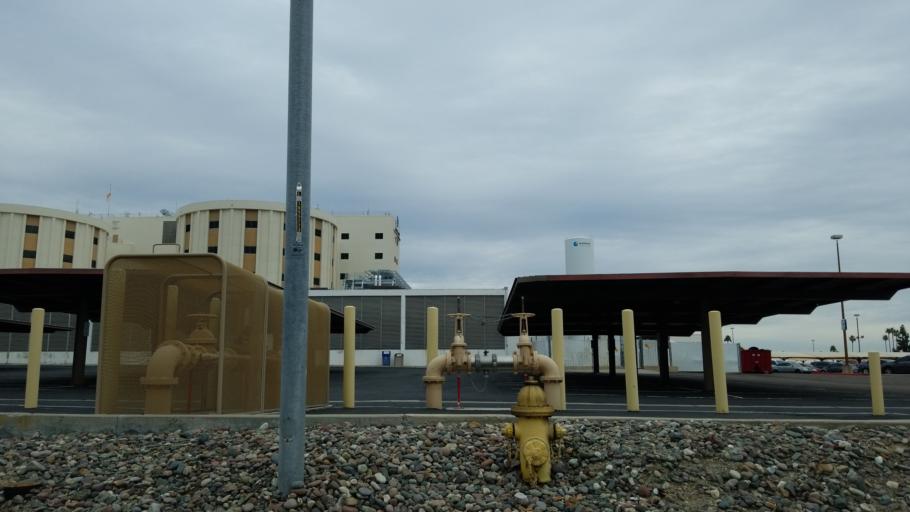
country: US
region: Arizona
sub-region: Maricopa County
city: Sun City
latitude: 33.6033
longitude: -112.2852
